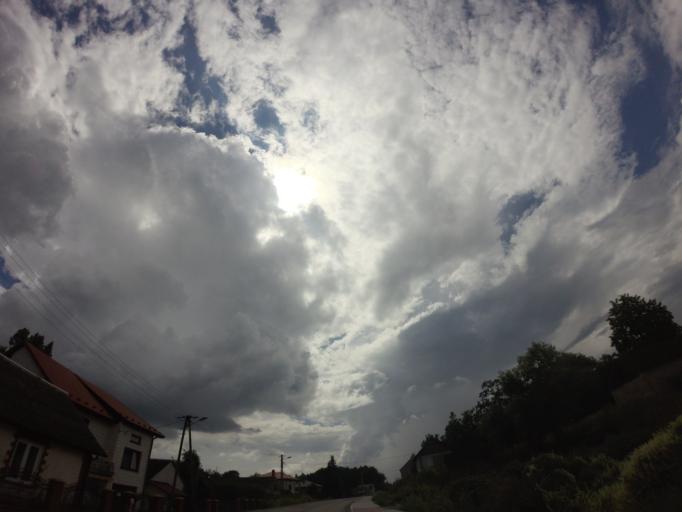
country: PL
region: Swietokrzyskie
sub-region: Powiat opatowski
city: Tarlow
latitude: 51.0368
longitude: 21.6920
